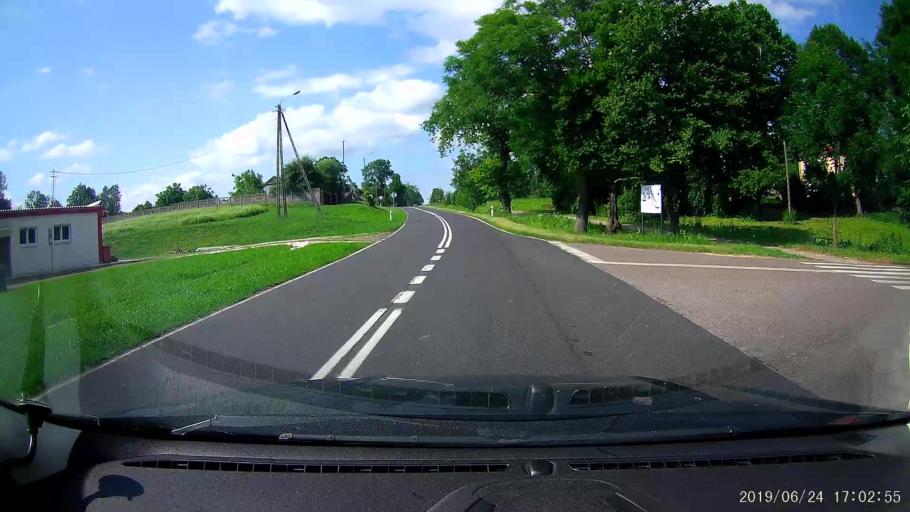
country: PL
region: Lublin Voivodeship
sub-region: Powiat tomaszowski
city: Telatyn
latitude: 50.5566
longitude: 23.9370
